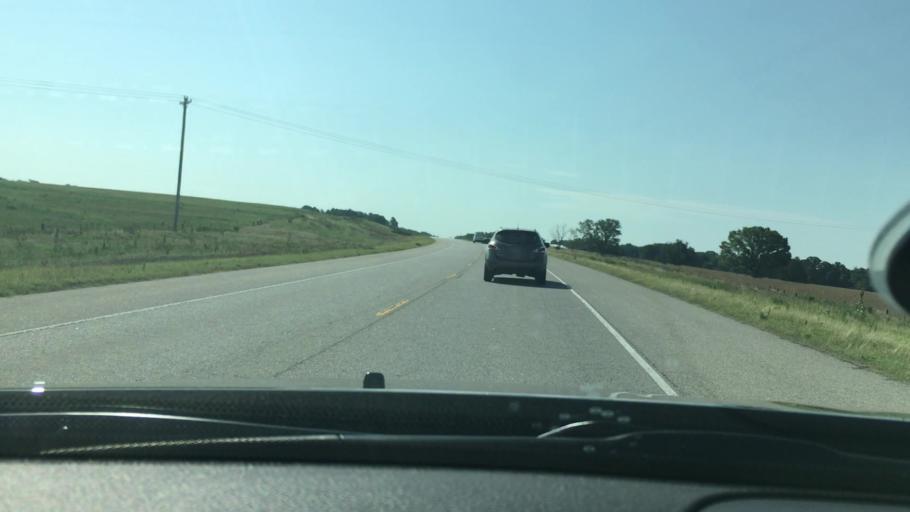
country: US
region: Oklahoma
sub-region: Pontotoc County
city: Ada
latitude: 34.6842
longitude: -96.5901
